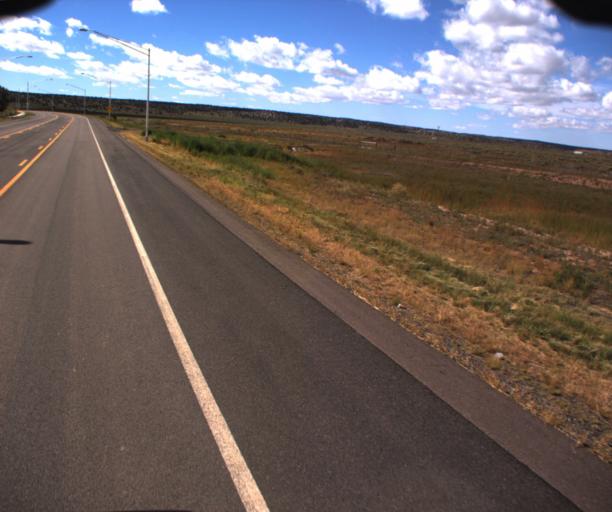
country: US
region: Arizona
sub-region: Apache County
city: Houck
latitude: 35.2071
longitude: -109.3315
